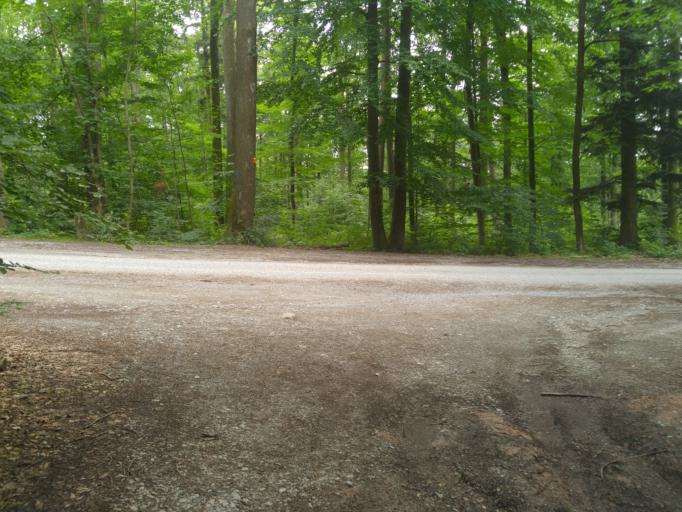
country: DE
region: Baden-Wuerttemberg
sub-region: Regierungsbezirk Stuttgart
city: Wustenrot
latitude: 49.0776
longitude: 9.4485
